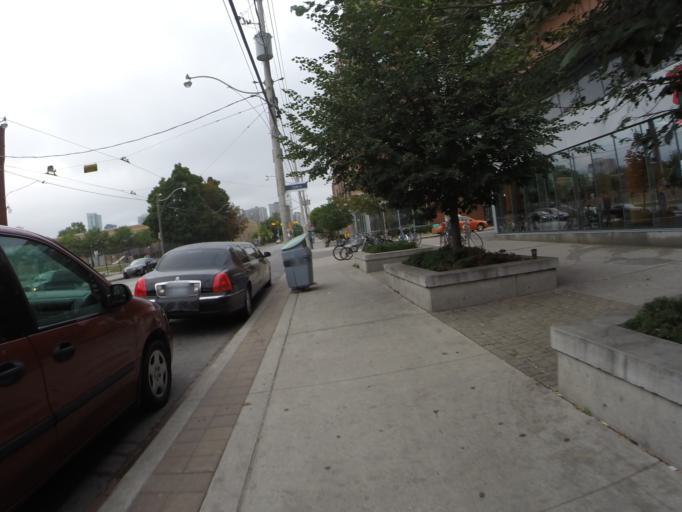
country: CA
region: Ontario
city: Toronto
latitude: 43.6587
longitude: -79.3656
